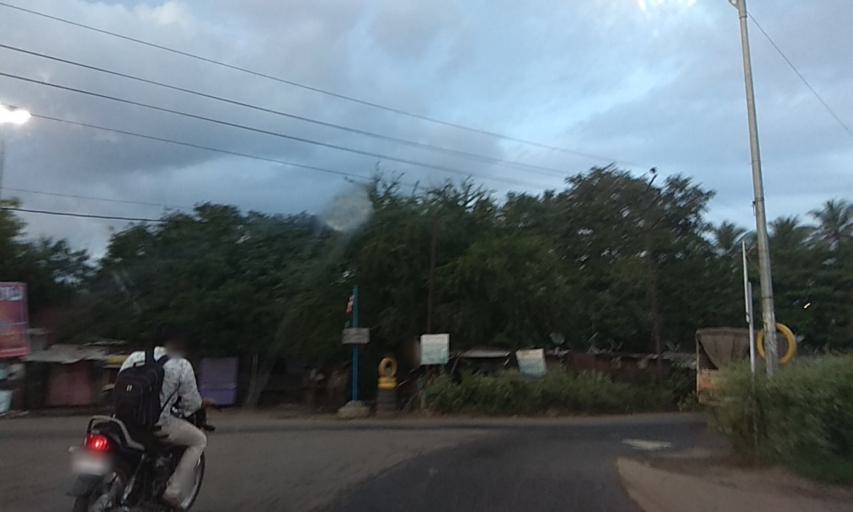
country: IN
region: Maharashtra
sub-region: Pune Division
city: Pune
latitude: 18.5197
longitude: 73.9157
